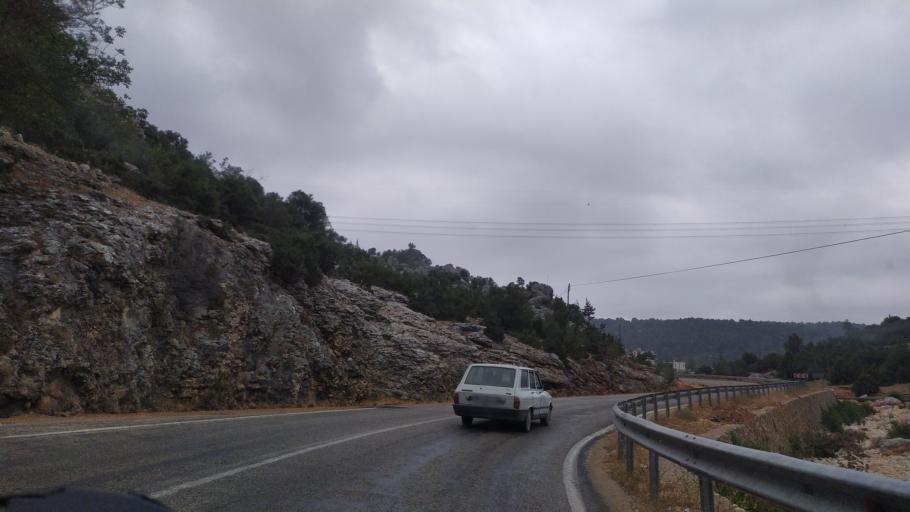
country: TR
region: Mersin
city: Silifke
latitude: 36.5328
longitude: 33.9426
